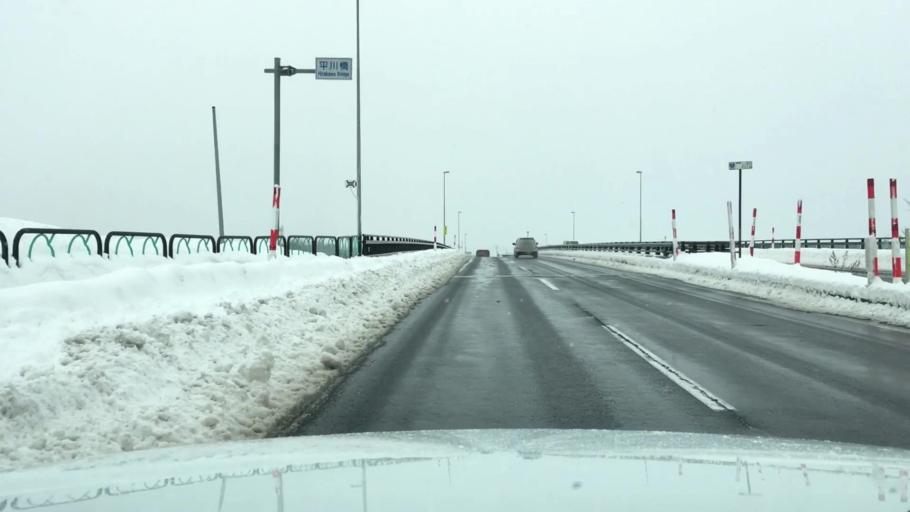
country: JP
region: Aomori
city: Hirosaki
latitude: 40.6441
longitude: 140.4948
